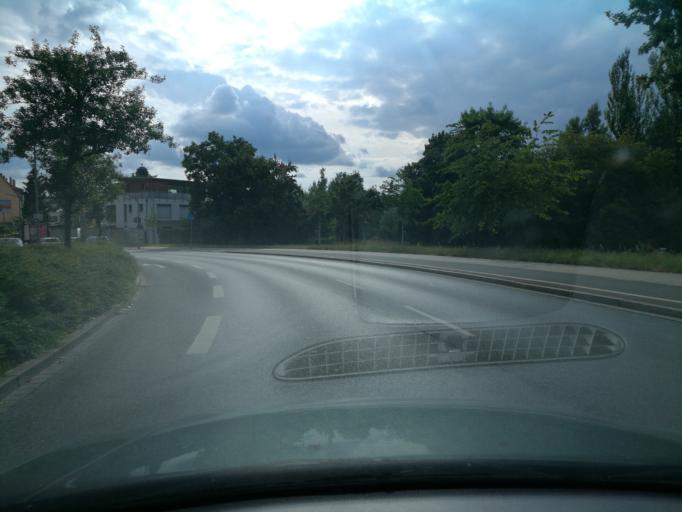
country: DE
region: Bavaria
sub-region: Regierungsbezirk Mittelfranken
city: Furth
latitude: 49.4833
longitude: 10.9820
